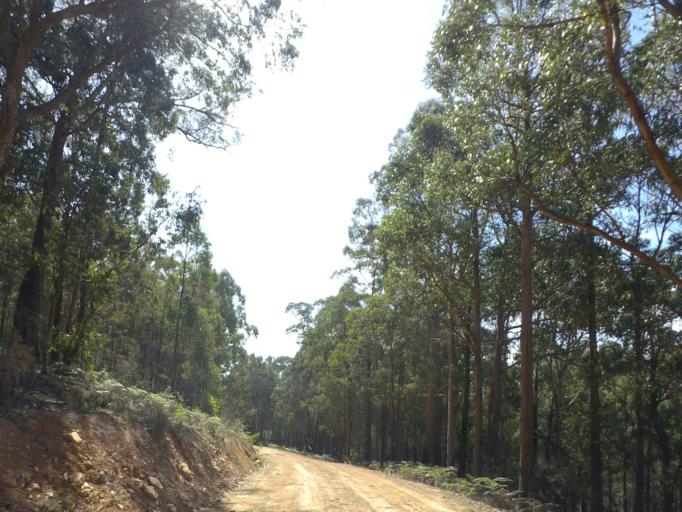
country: AU
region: Victoria
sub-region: Moorabool
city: Bacchus Marsh
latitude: -37.4380
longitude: 144.3650
